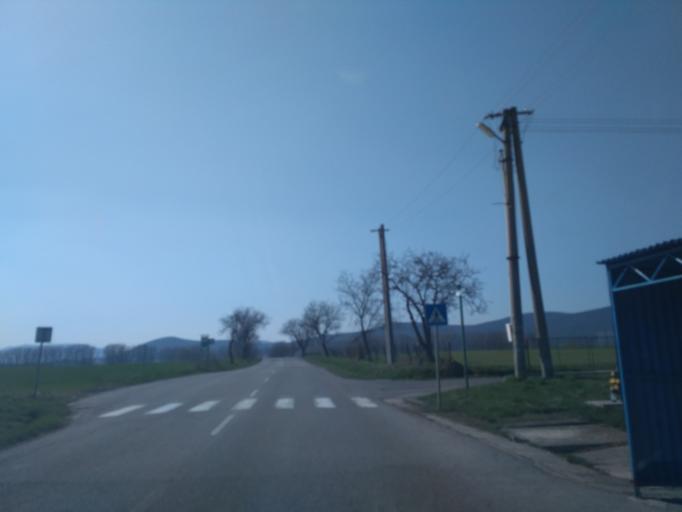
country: SK
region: Kosicky
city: Secovce
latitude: 48.6589
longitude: 21.6066
